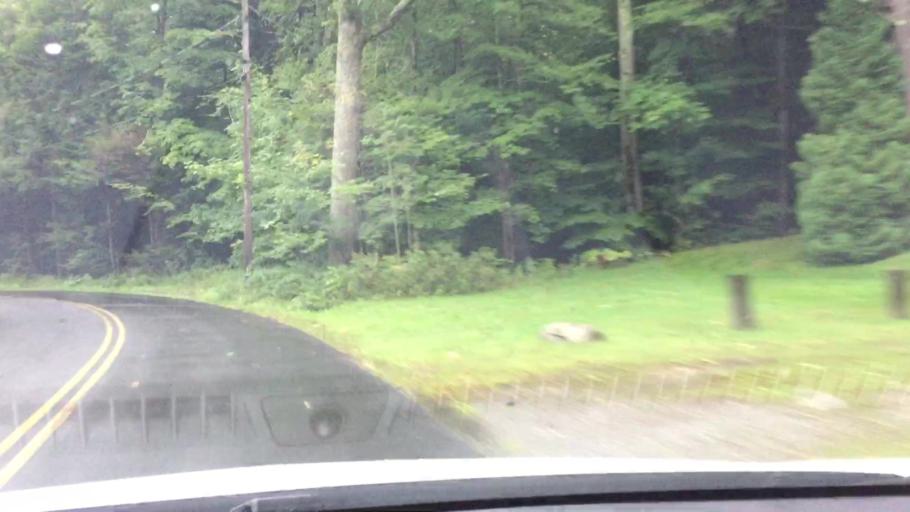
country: US
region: Massachusetts
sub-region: Berkshire County
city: Otis
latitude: 42.1502
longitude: -73.0545
